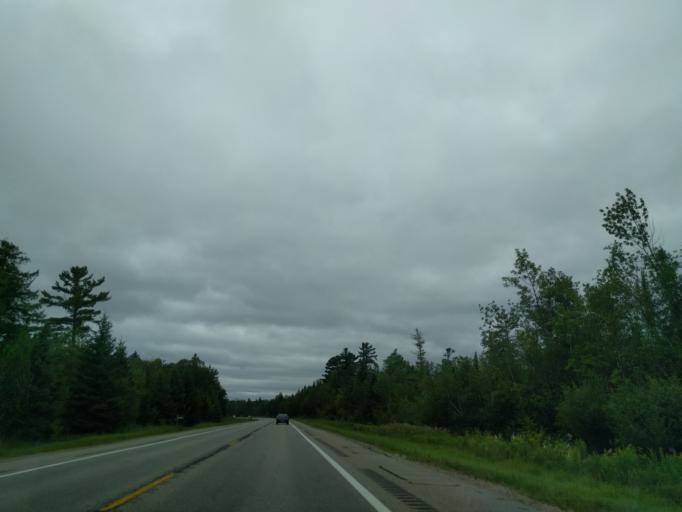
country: US
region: Michigan
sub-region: Delta County
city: Escanaba
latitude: 45.6693
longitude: -87.1587
